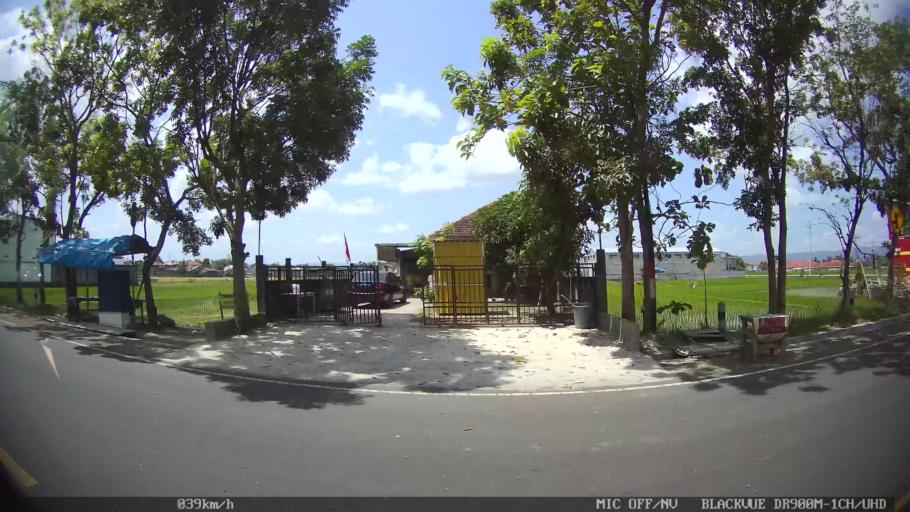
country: ID
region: Daerah Istimewa Yogyakarta
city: Bantul
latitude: -7.9010
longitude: 110.3459
